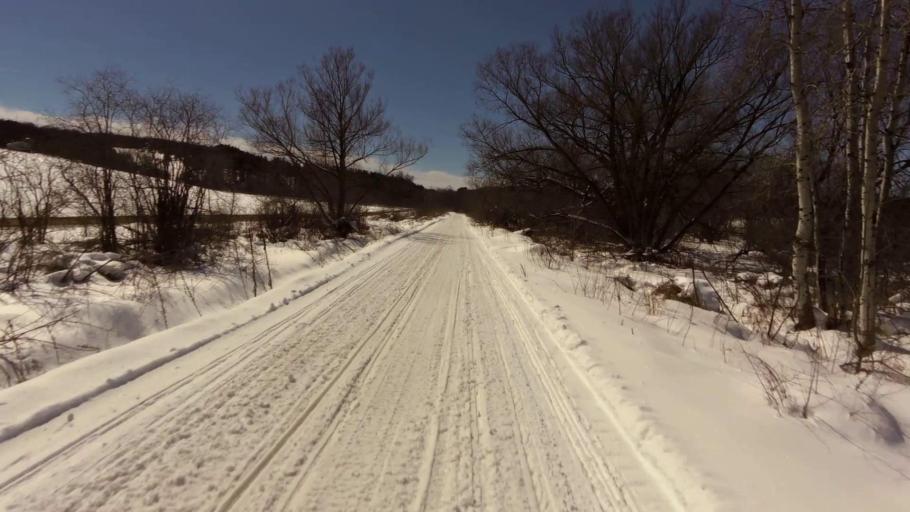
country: US
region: New York
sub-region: Cattaraugus County
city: Delevan
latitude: 42.4322
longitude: -78.4463
